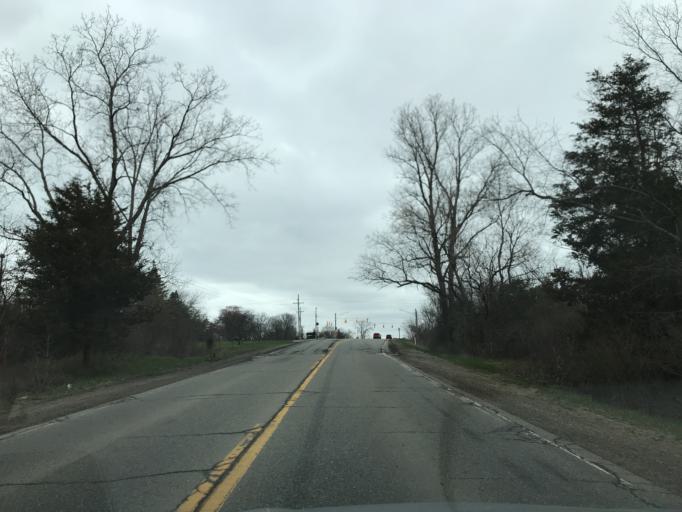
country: US
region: Michigan
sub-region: Oakland County
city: South Lyon
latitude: 42.5160
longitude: -83.6899
